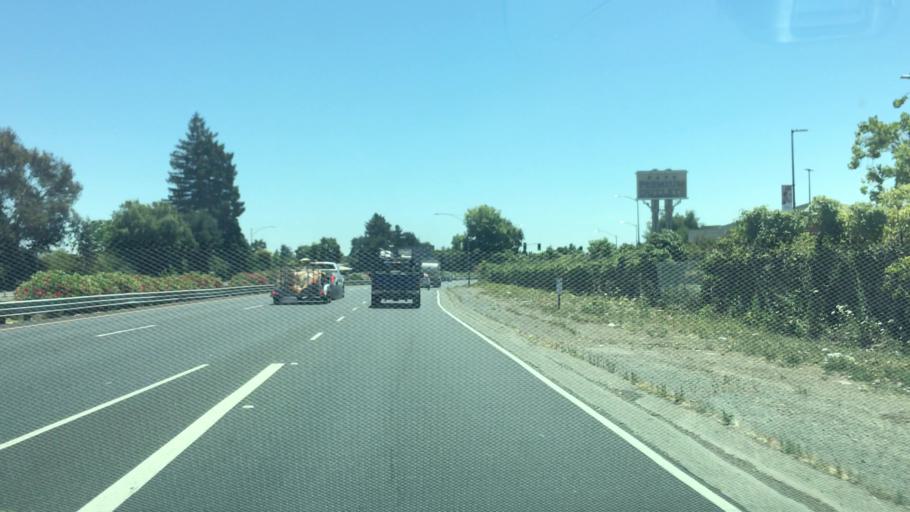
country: US
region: California
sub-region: Napa County
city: Napa
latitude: 38.2979
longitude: -122.3023
